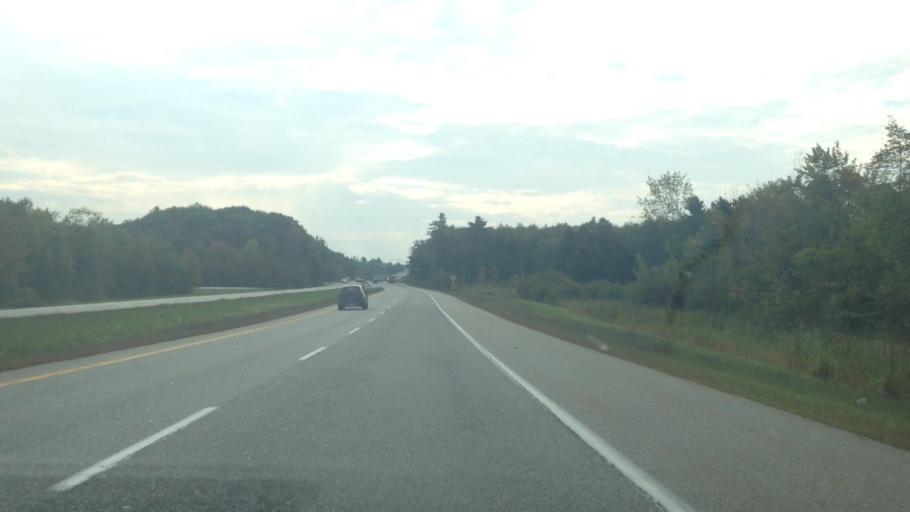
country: US
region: Maine
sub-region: Cumberland County
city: Westbrook
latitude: 43.6724
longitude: -70.3414
